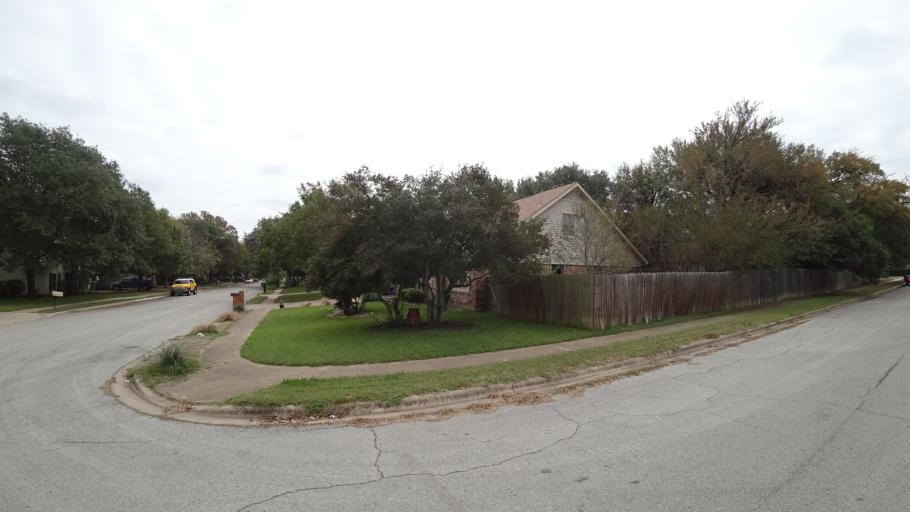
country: US
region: Texas
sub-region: Travis County
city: Wells Branch
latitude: 30.4329
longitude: -97.7179
